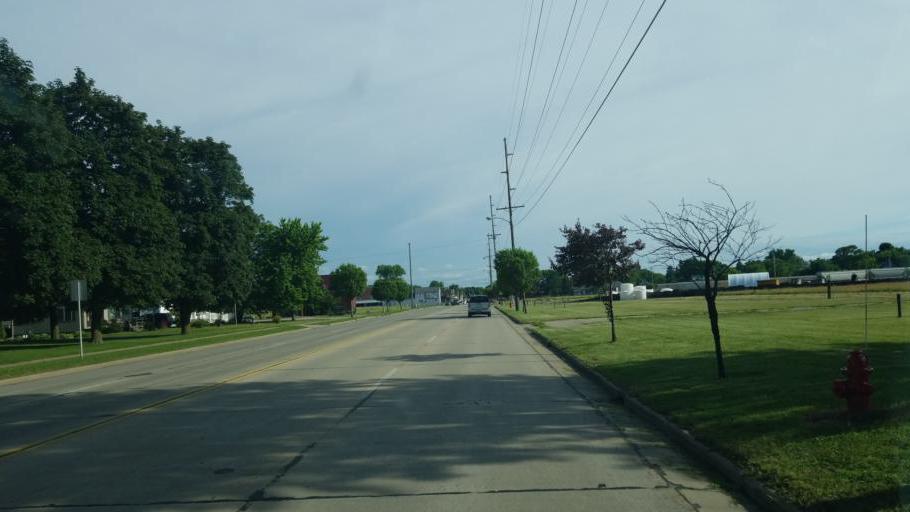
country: US
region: Wisconsin
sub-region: Monroe County
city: Tomah
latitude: 43.9895
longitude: -90.5047
